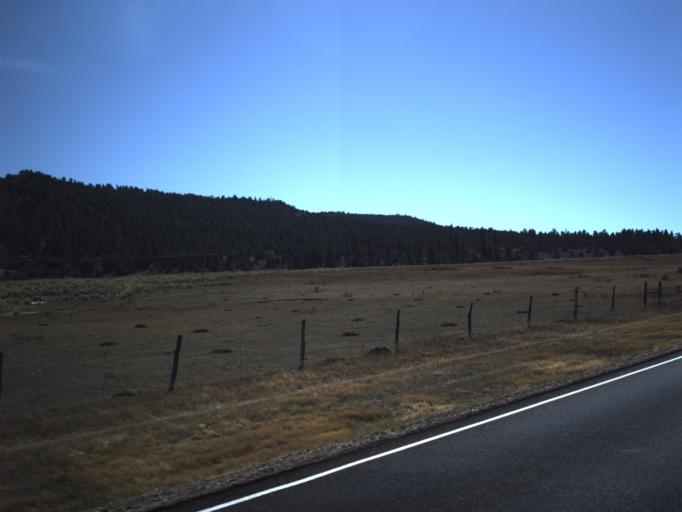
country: US
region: Utah
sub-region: Garfield County
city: Panguitch
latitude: 37.6797
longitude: -111.8178
